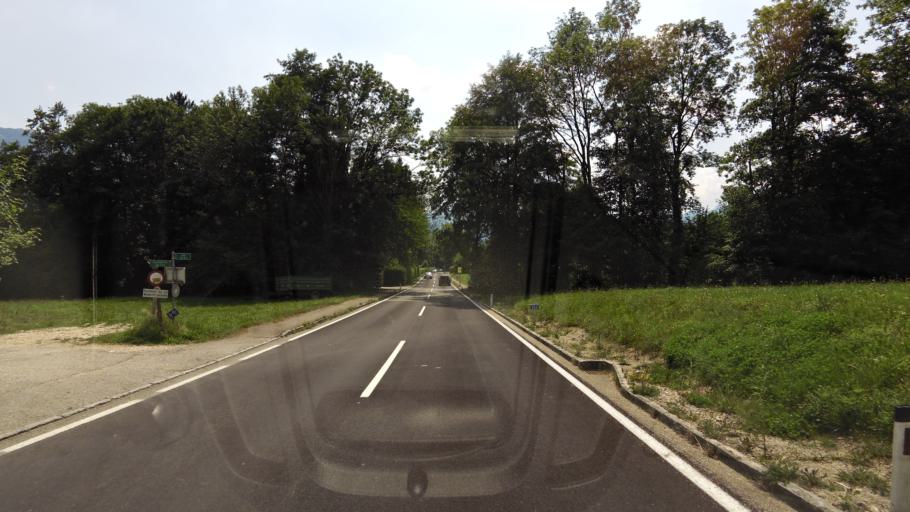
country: AT
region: Upper Austria
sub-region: Politischer Bezirk Vocklabruck
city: Steinbach am Attersee
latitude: 47.8492
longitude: 13.5263
